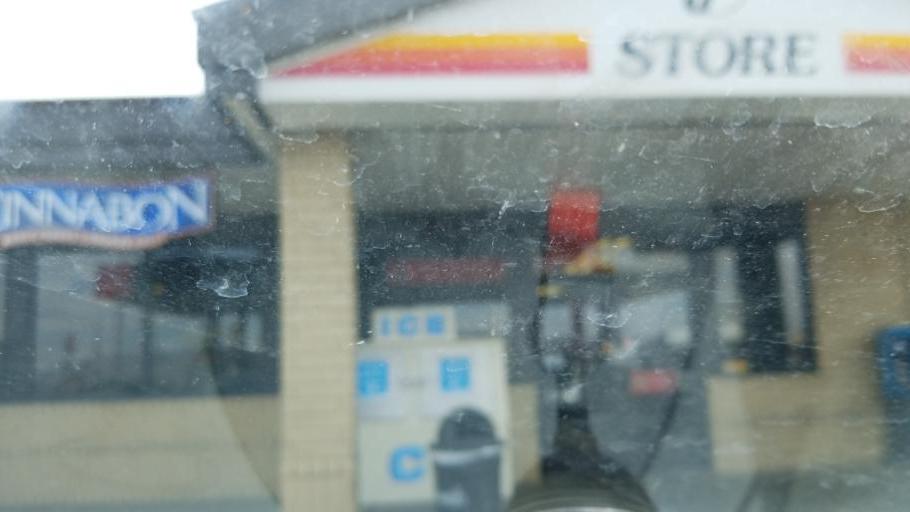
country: US
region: Arizona
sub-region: Mohave County
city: New Kingman-Butler
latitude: 35.2196
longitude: -114.0074
